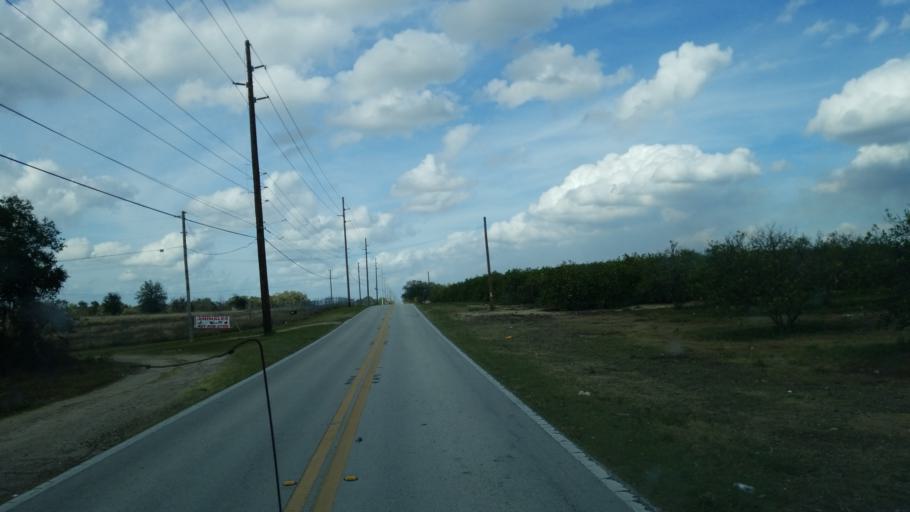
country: US
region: Florida
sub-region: Polk County
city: Haines City
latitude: 28.1244
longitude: -81.5904
